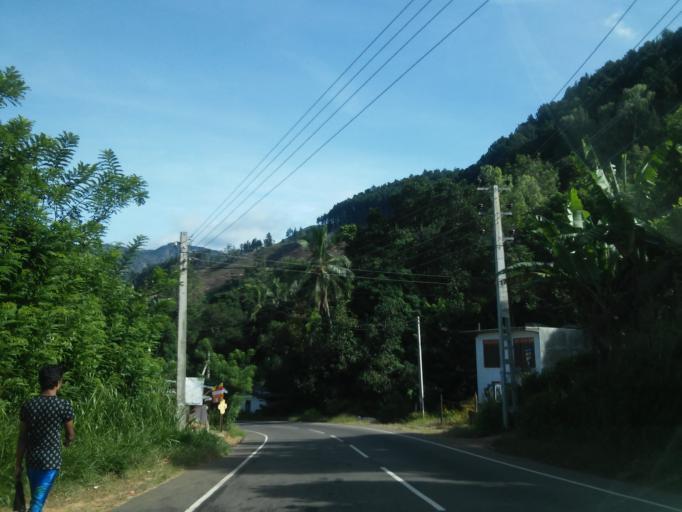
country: LK
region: Uva
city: Haputale
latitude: 6.7616
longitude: 80.8756
